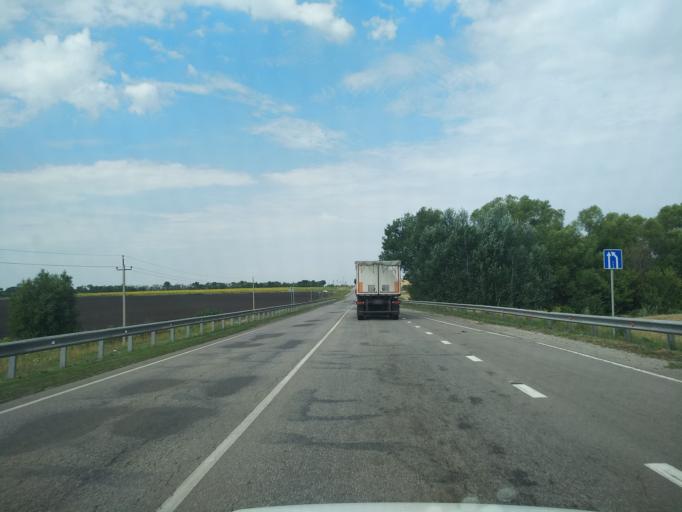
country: RU
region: Voronezj
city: Verkhnyaya Khava
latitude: 51.6778
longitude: 39.8614
